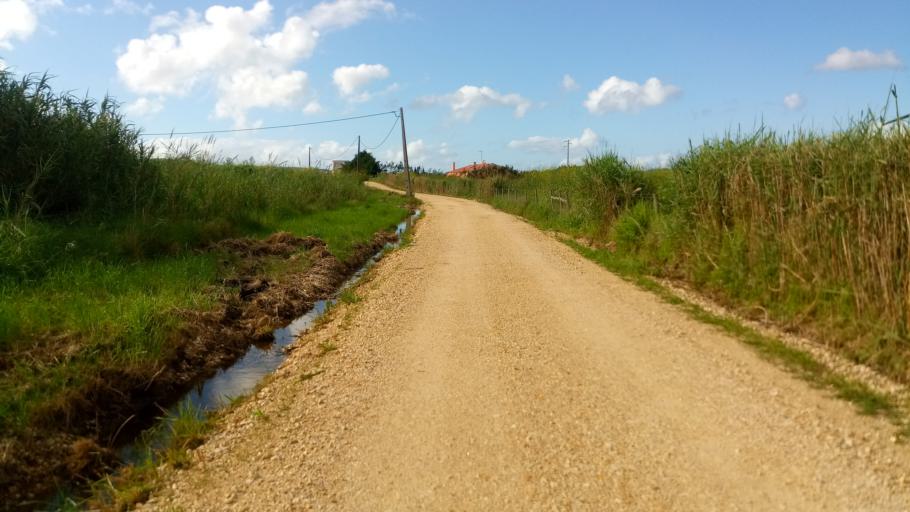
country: PT
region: Leiria
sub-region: Caldas da Rainha
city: Caldas da Rainha
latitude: 39.4314
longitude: -9.1606
